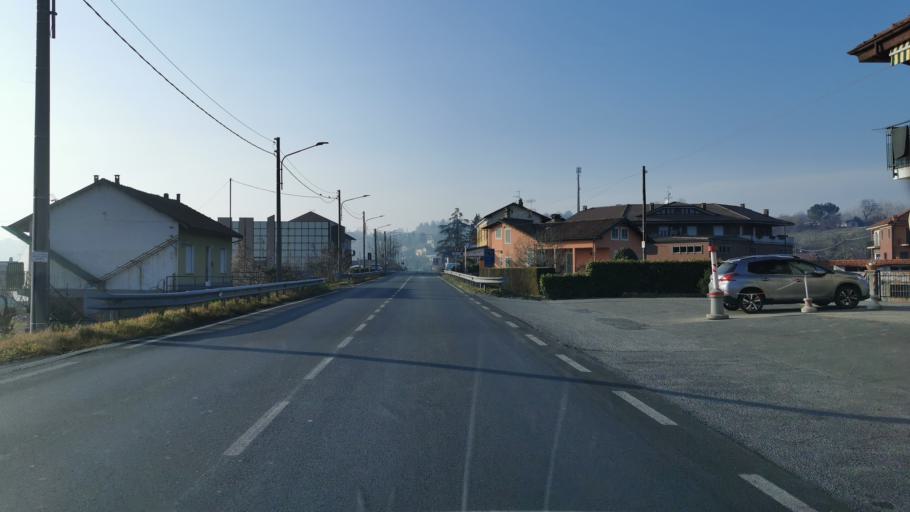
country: IT
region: Piedmont
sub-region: Provincia di Cuneo
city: Pocapaglia
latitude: 44.6976
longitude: 7.8849
